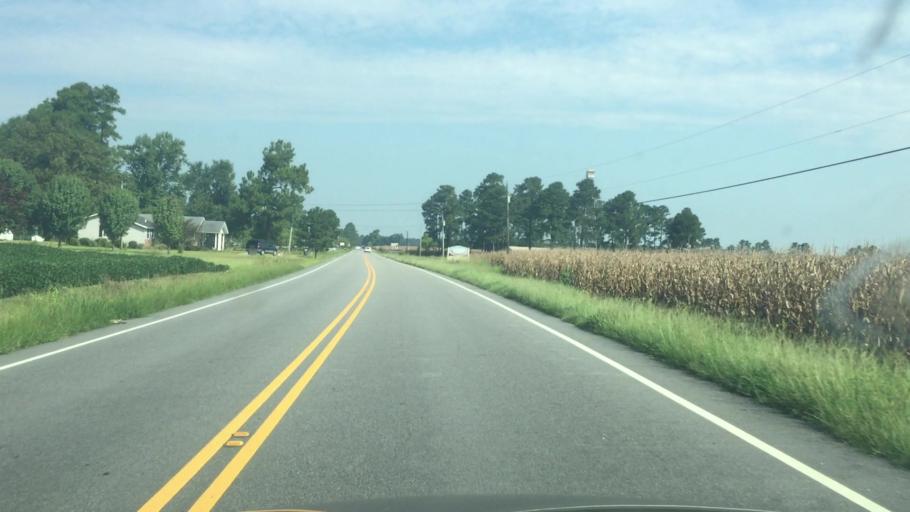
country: US
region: North Carolina
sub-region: Columbus County
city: Chadbourn
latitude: 34.2767
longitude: -78.8140
